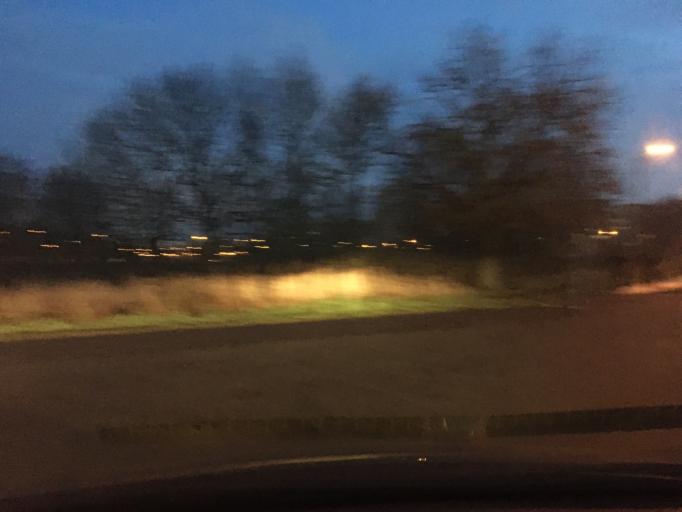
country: EE
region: Harju
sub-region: Viimsi vald
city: Viimsi
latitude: 59.4432
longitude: 24.8182
